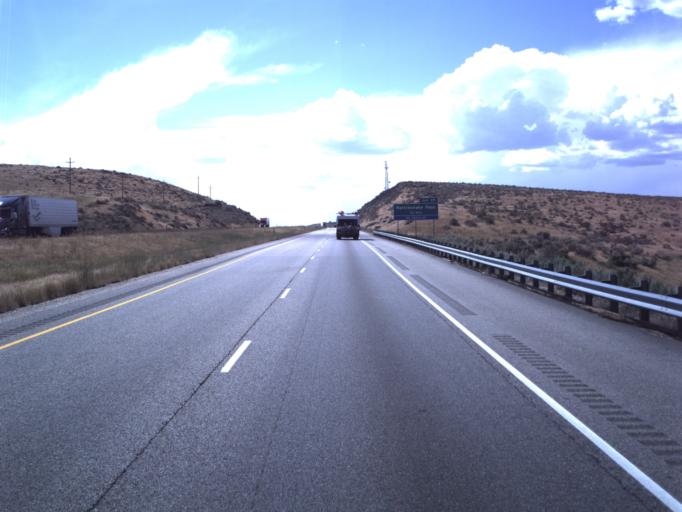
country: US
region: Utah
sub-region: Box Elder County
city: Garland
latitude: 41.8951
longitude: -112.5273
